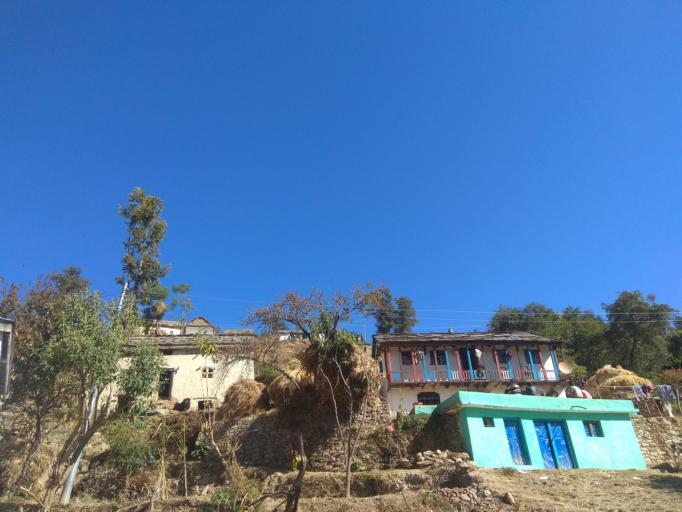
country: NP
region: Far Western
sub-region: Seti Zone
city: Achham
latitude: 29.2601
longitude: 81.6115
